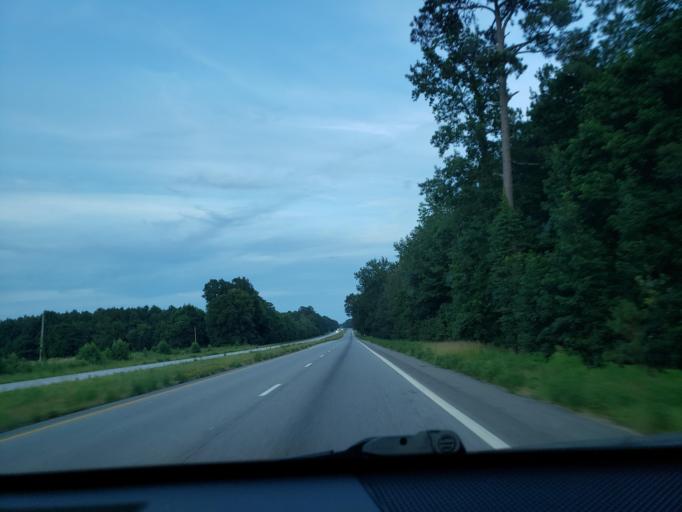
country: US
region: Virginia
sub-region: Southampton County
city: Courtland
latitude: 36.7076
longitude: -77.1678
